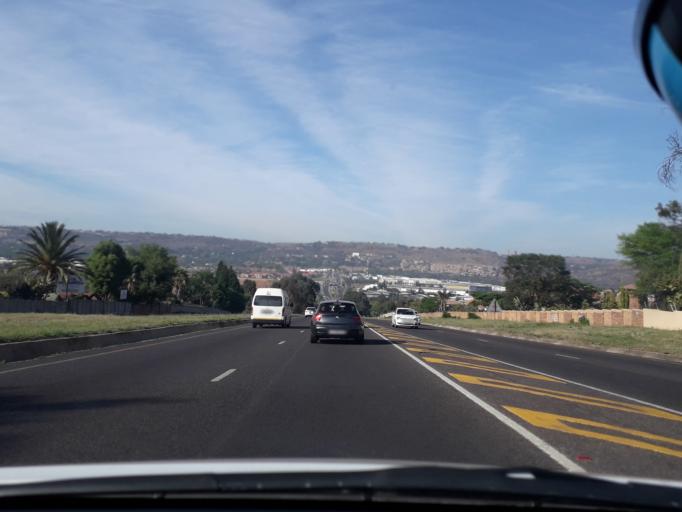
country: ZA
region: Gauteng
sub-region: City of Johannesburg Metropolitan Municipality
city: Roodepoort
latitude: -26.1142
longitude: 27.9178
